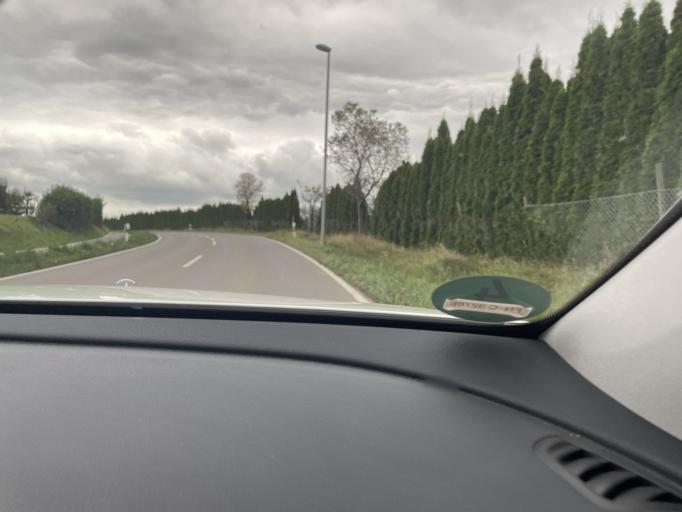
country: DE
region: Baden-Wuerttemberg
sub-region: Tuebingen Region
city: Friedrichshafen
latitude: 47.6813
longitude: 9.4430
